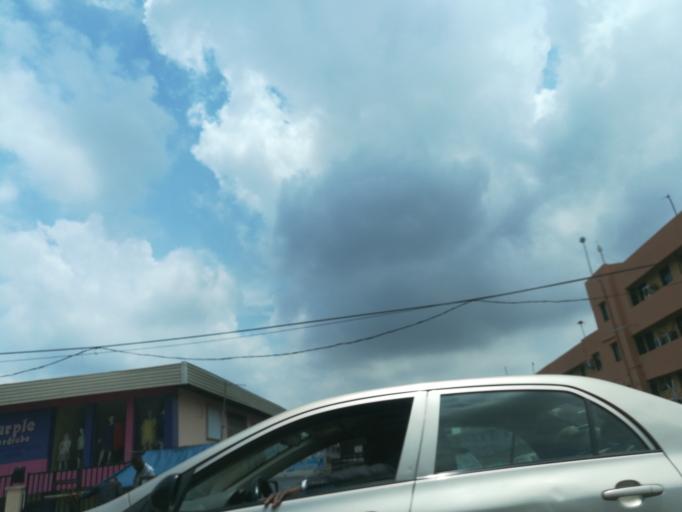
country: NG
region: Lagos
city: Oshodi
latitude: 6.5468
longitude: 3.3326
